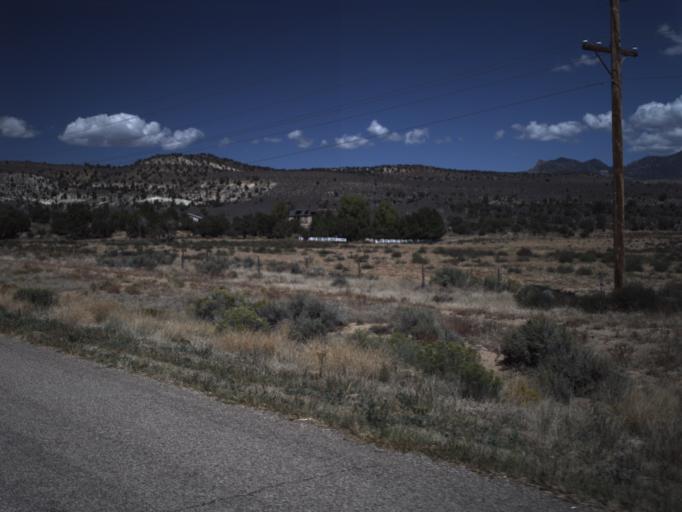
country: US
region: Utah
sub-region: Washington County
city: Ivins
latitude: 37.2638
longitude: -113.6362
